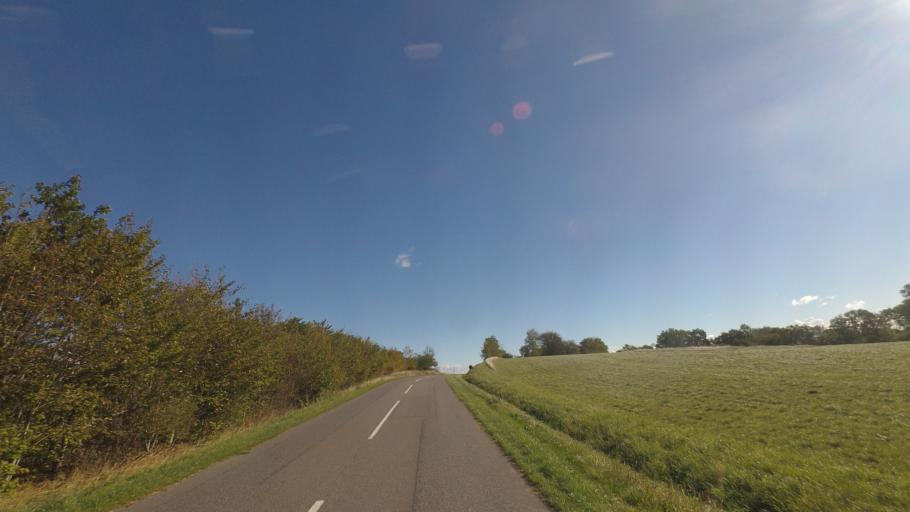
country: DK
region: Capital Region
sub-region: Bornholm Kommune
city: Nexo
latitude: 55.0786
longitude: 15.0981
